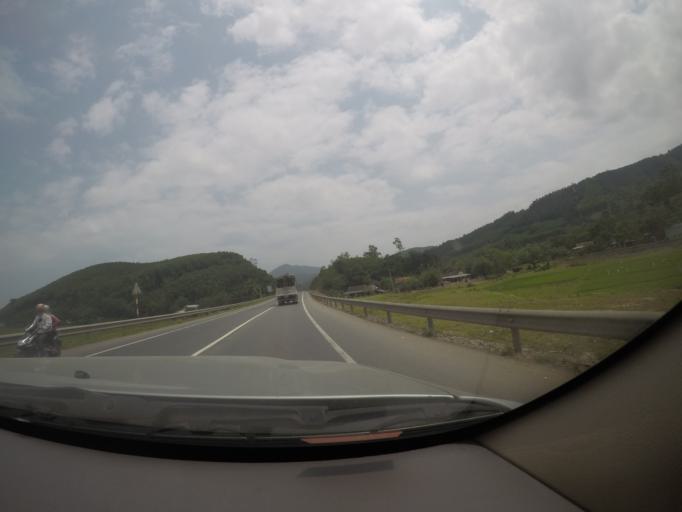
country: VN
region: Thua Thien-Hue
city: Phu Loc
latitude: 16.2783
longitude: 107.9001
